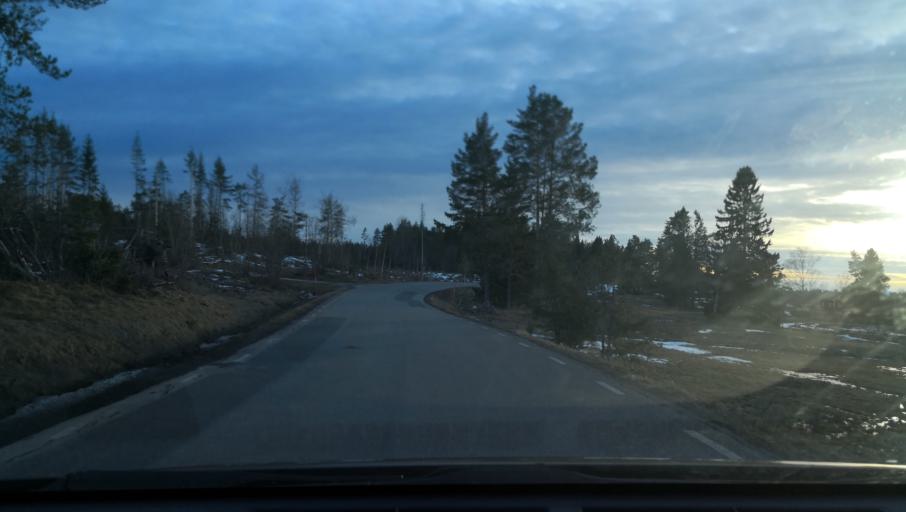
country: SE
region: Uppsala
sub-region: Osthammars Kommun
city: Osterbybruk
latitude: 60.2506
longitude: 17.9432
